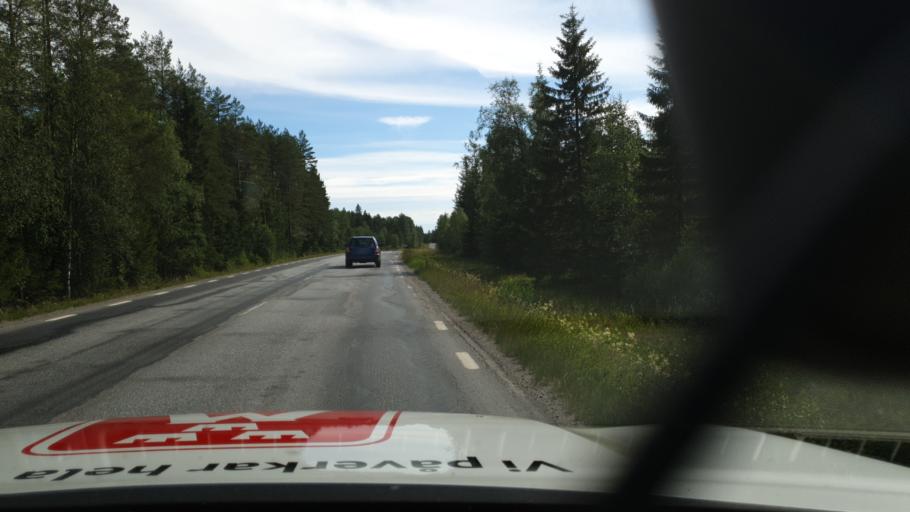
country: SE
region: Vaesterbotten
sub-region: Umea Kommun
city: Roback
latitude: 63.8807
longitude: 20.1992
